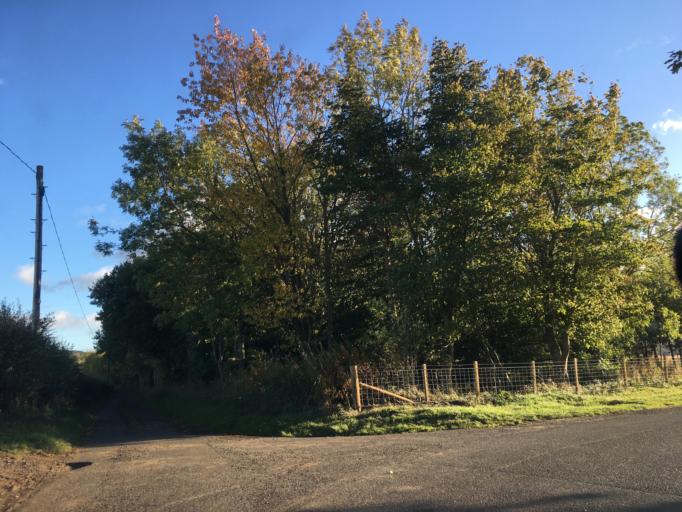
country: GB
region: Scotland
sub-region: Fife
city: Pathhead
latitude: 55.8478
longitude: -2.9163
